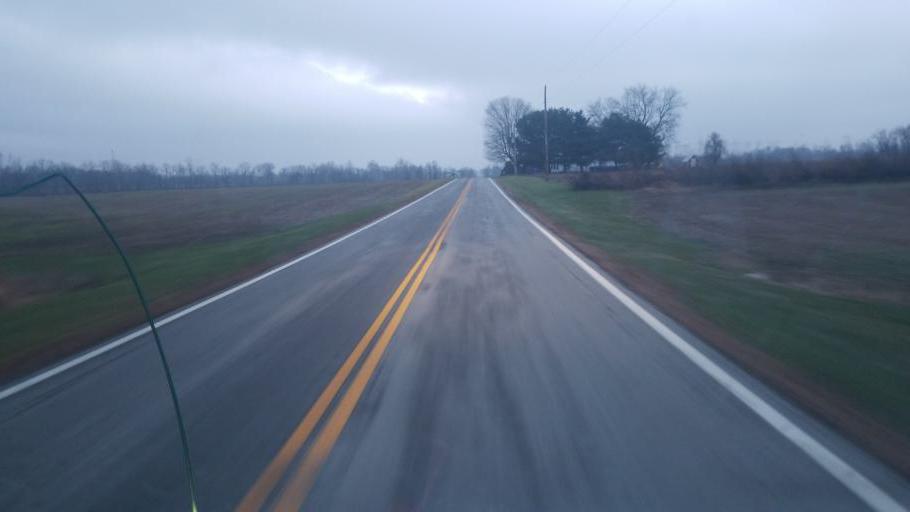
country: US
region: Ohio
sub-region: Wyandot County
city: Upper Sandusky
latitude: 40.8557
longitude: -83.1316
